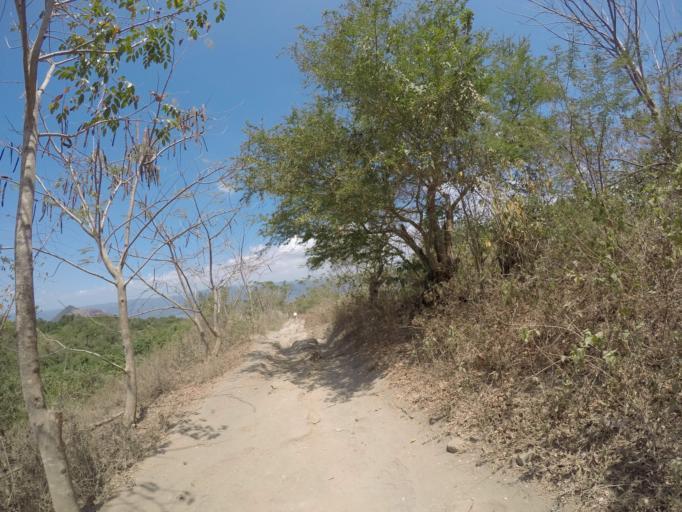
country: PH
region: Calabarzon
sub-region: Province of Batangas
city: Bugaan
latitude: 14.0234
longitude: 120.9992
